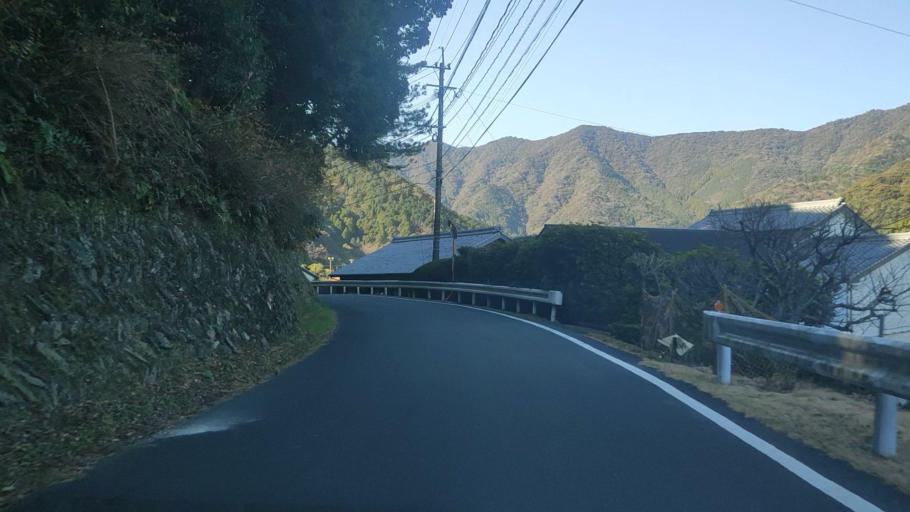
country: JP
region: Oita
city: Saiki
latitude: 32.8342
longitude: 131.9466
